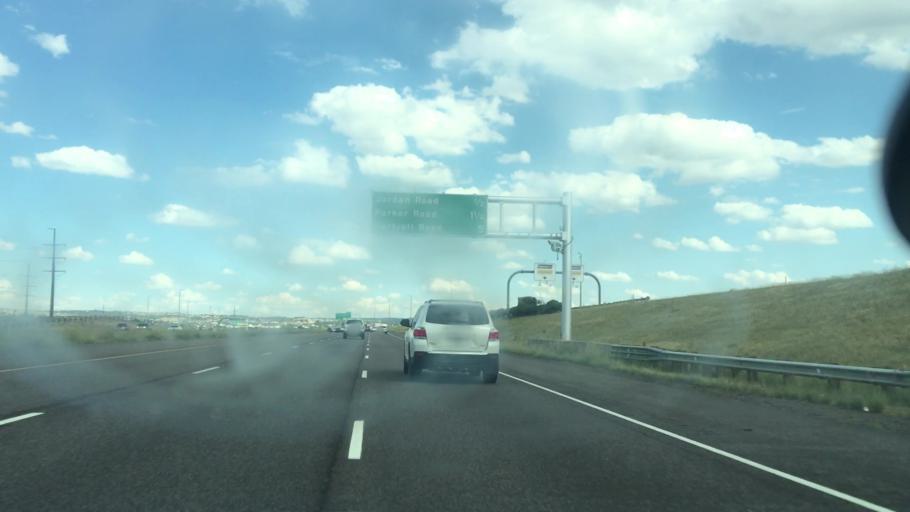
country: US
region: Colorado
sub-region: Douglas County
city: Stonegate
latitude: 39.5523
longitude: -104.8070
